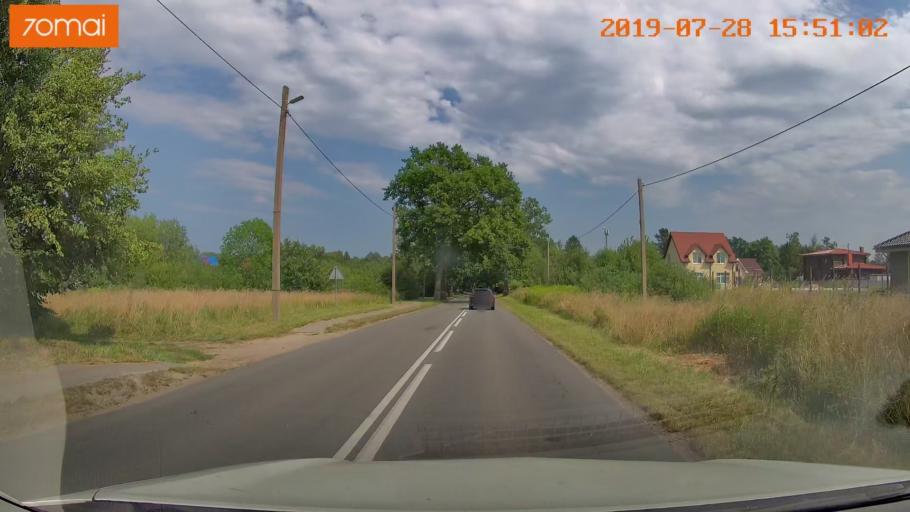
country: RU
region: Kaliningrad
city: Otradnoye
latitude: 54.9417
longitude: 20.0995
